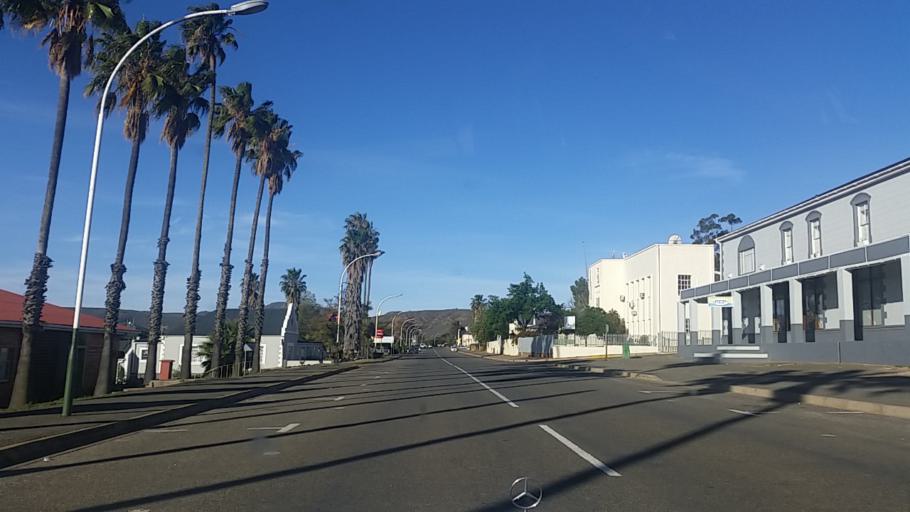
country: ZA
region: Western Cape
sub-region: Eden District Municipality
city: Knysna
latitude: -33.6566
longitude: 23.1265
